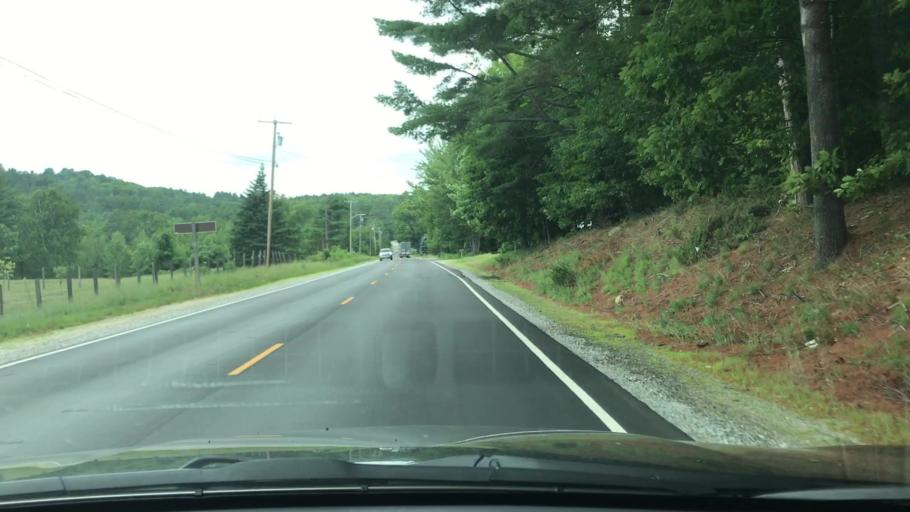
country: US
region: Maine
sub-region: Oxford County
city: West Paris
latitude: 44.3856
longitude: -70.6550
